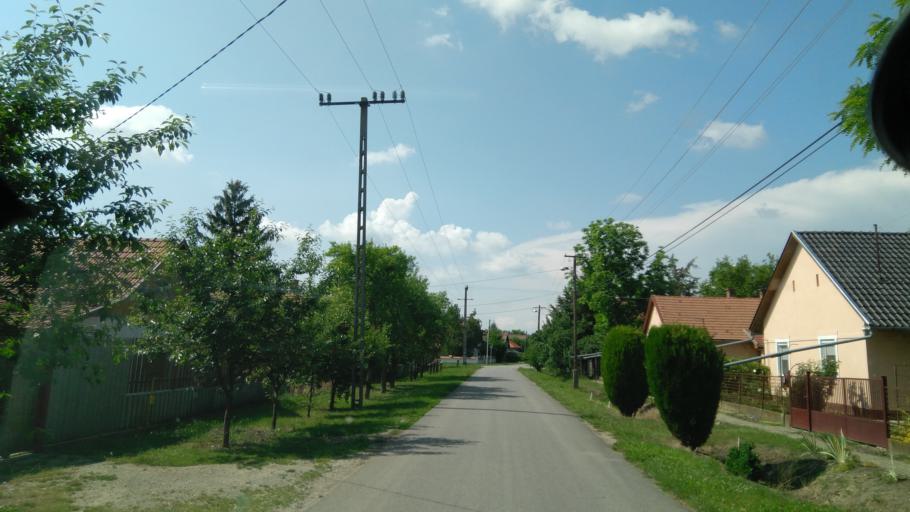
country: HU
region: Bekes
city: Doboz
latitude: 46.7359
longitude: 21.2301
